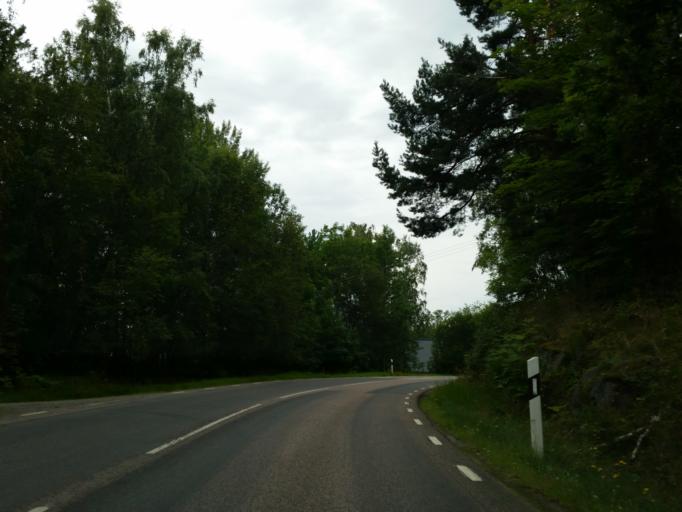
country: SE
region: Stockholm
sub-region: Sodertalje Kommun
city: Soedertaelje
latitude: 59.2003
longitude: 17.5422
